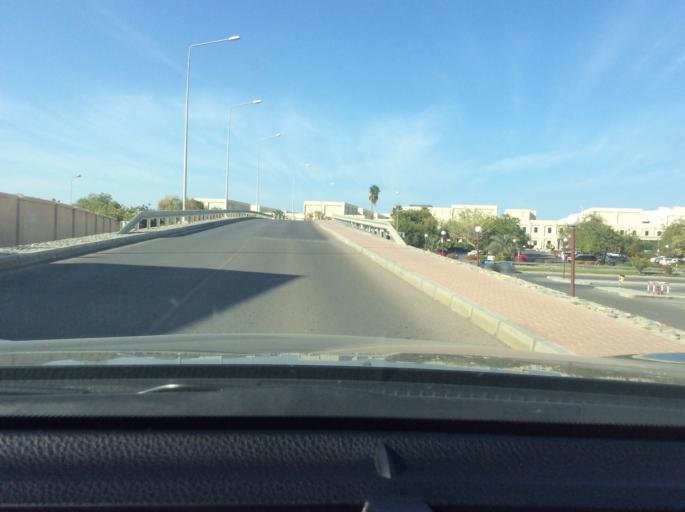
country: OM
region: Muhafazat Masqat
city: As Sib al Jadidah
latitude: 23.5857
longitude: 58.1711
